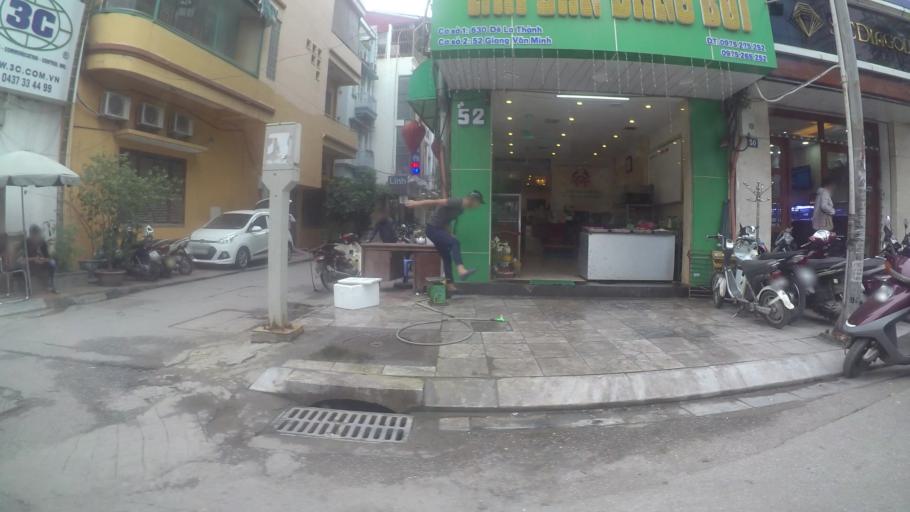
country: VN
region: Ha Noi
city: Dong Da
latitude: 21.0340
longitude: 105.8271
